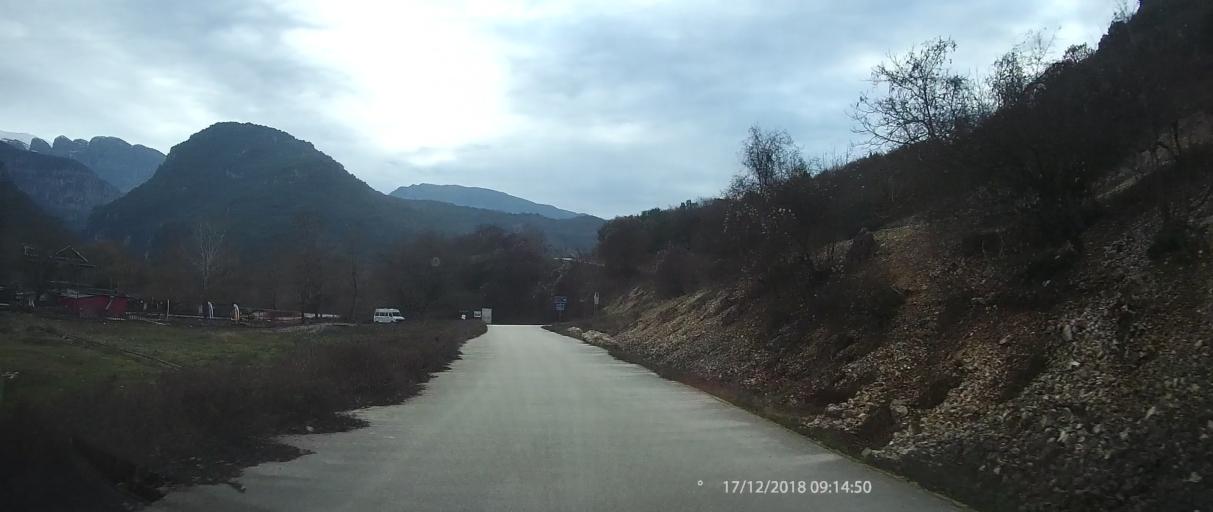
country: GR
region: Epirus
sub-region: Nomos Ioanninon
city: Kalpaki
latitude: 39.9699
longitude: 20.6551
